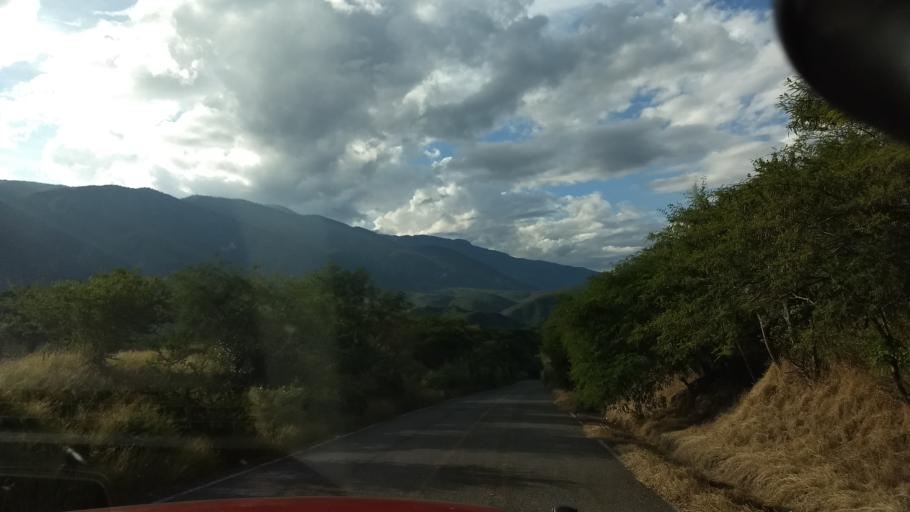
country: MX
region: Colima
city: Suchitlan
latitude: 19.4494
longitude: -103.8178
